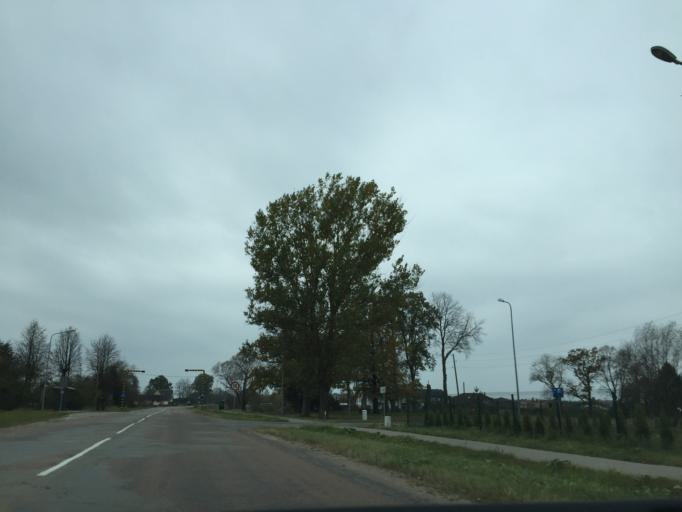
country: LV
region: Marupe
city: Marupe
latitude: 56.8466
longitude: 24.0476
